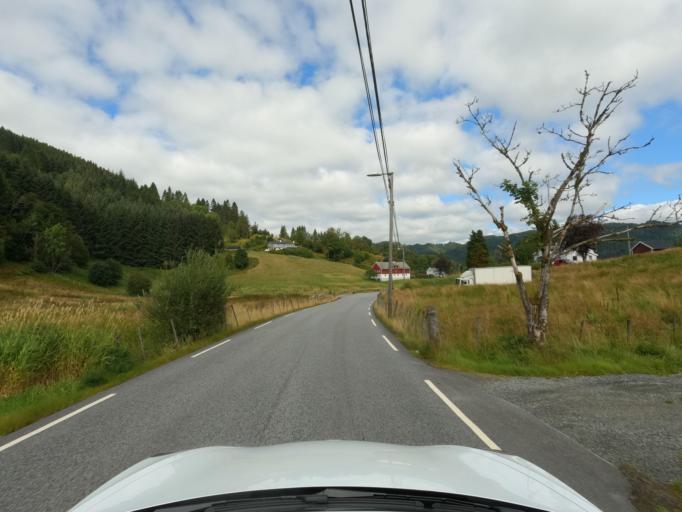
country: NO
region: Hordaland
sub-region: Os
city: Syfteland
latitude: 60.2765
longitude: 5.3747
